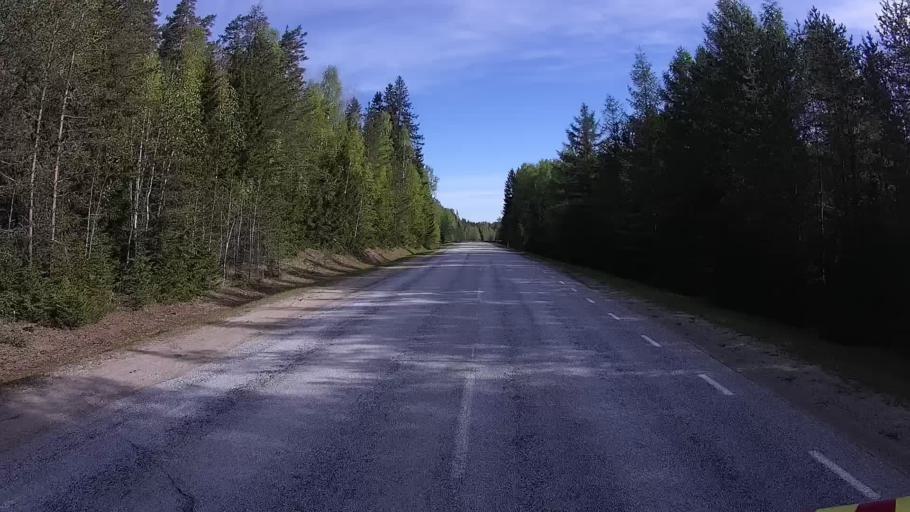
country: EE
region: Tartu
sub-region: Elva linn
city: Elva
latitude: 58.0943
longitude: 26.4923
